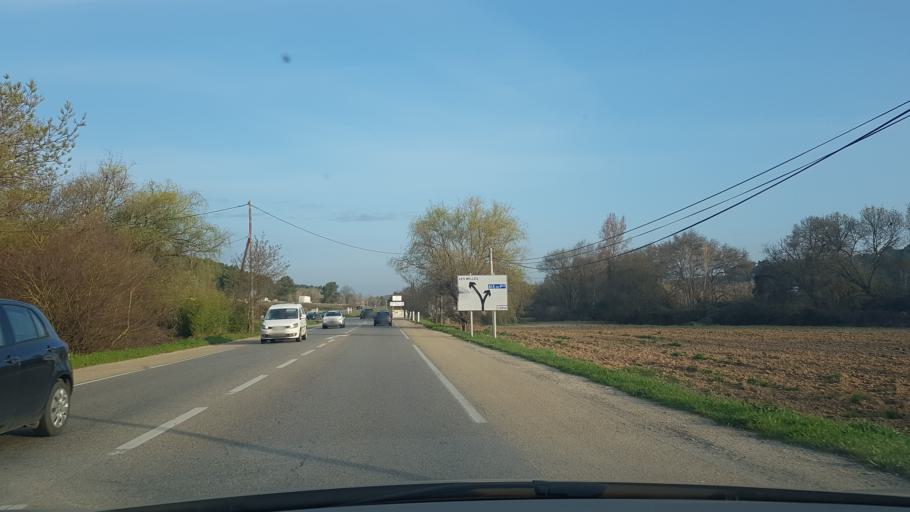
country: FR
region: Provence-Alpes-Cote d'Azur
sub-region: Departement des Bouches-du-Rhone
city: Bouc-Bel-Air
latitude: 43.4880
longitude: 5.4094
